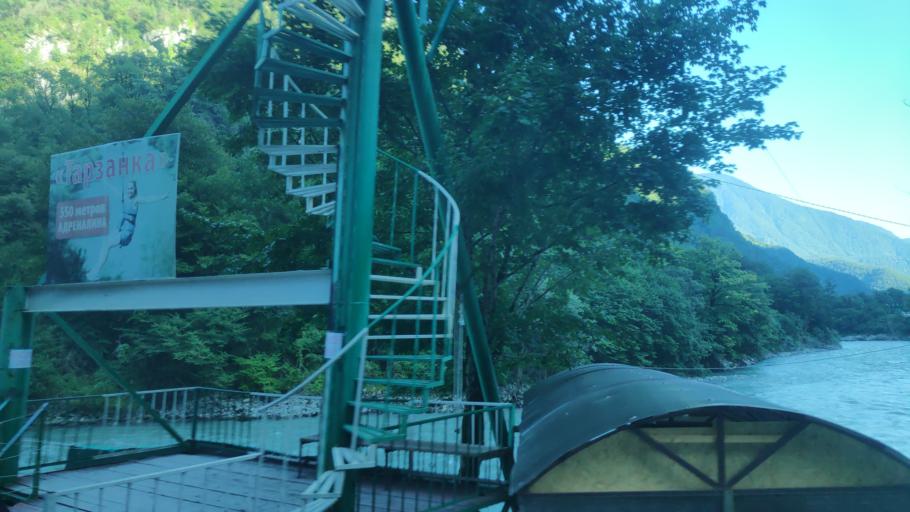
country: GE
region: Abkhazia
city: Gagra
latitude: 43.3510
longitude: 40.4125
